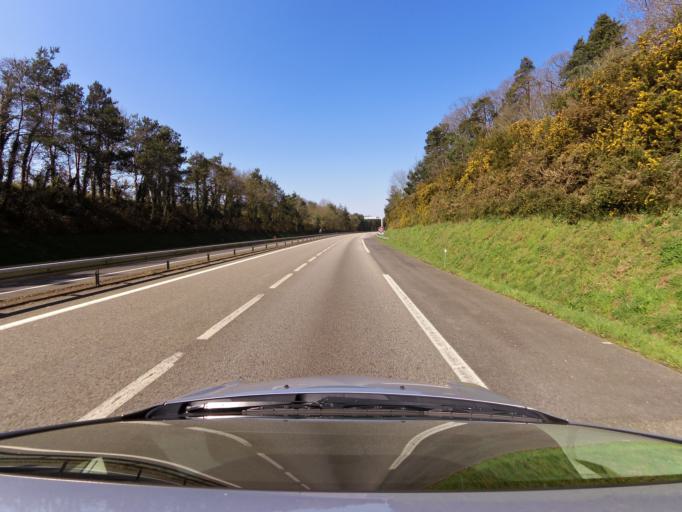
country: FR
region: Brittany
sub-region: Departement du Morbihan
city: Guillac
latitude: 47.9367
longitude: -2.4858
